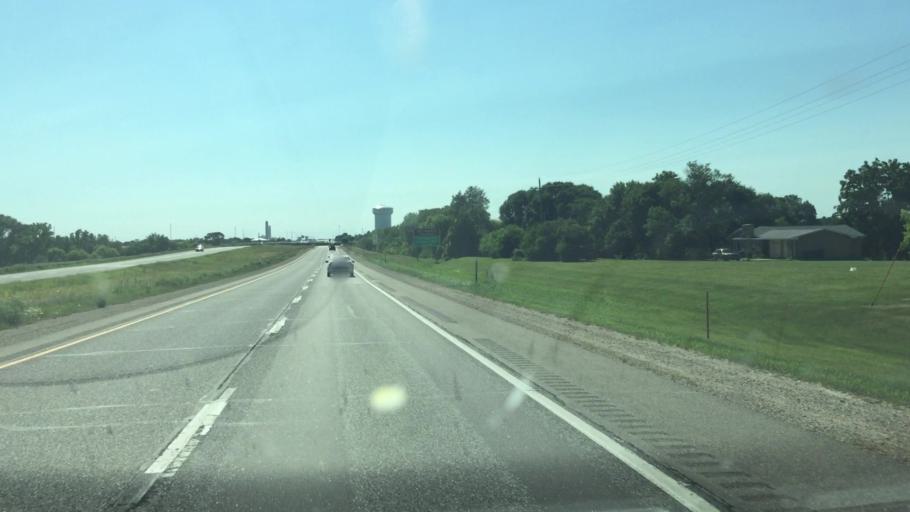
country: US
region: Iowa
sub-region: Linn County
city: Ely
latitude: 41.9266
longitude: -91.6272
